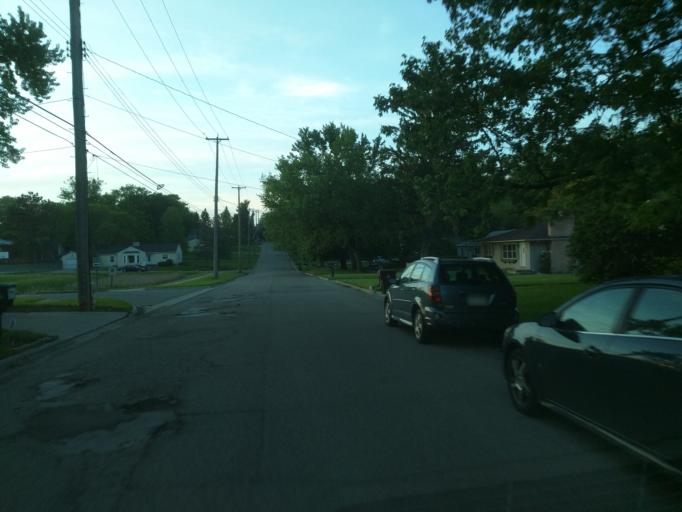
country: US
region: Michigan
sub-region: Eaton County
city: Waverly
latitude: 42.7459
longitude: -84.6090
